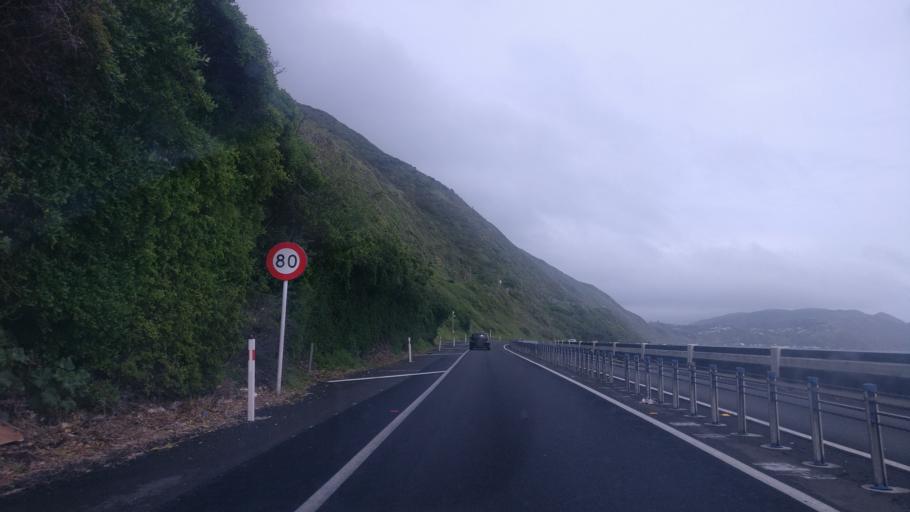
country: NZ
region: Wellington
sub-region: Kapiti Coast District
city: Paraparaumu
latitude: -41.0129
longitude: 174.9202
